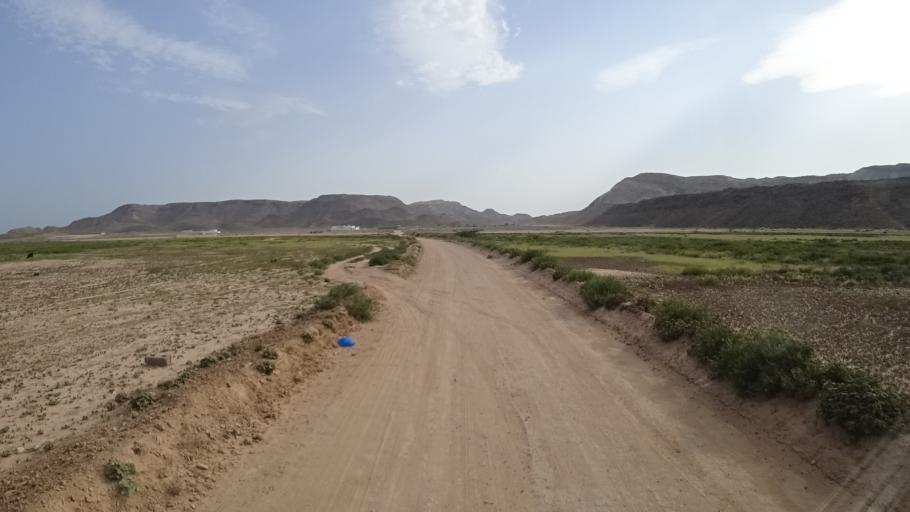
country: OM
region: Ash Sharqiyah
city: Sur
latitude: 22.4436
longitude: 59.8227
